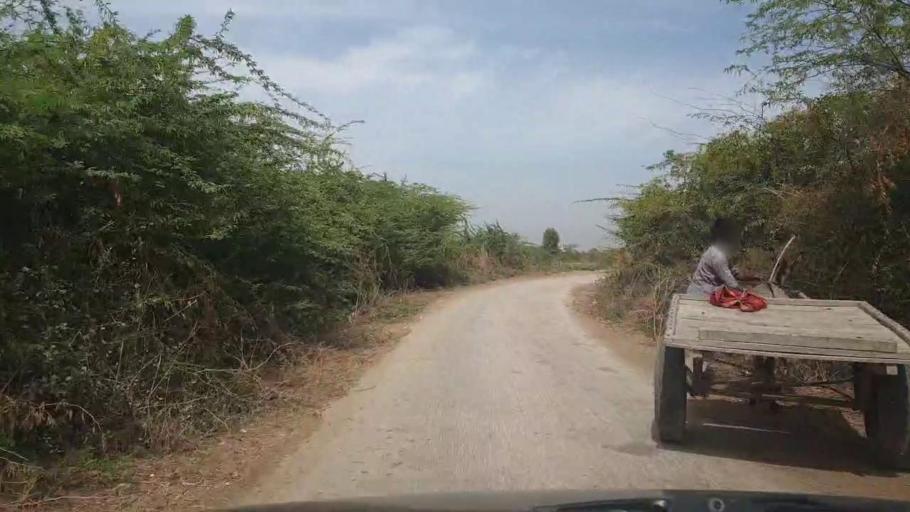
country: PK
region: Sindh
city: Kunri
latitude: 25.2346
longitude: 69.6697
